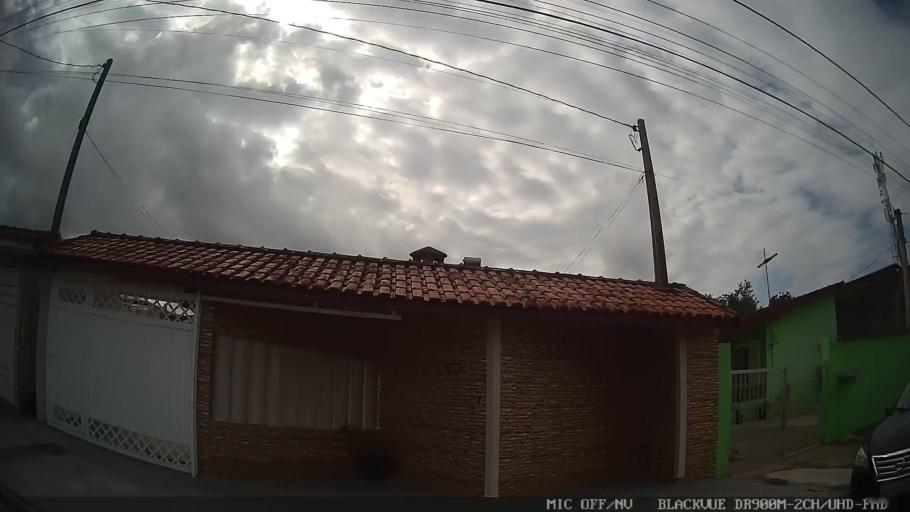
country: BR
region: Sao Paulo
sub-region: Itanhaem
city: Itanhaem
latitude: -24.1968
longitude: -46.8199
